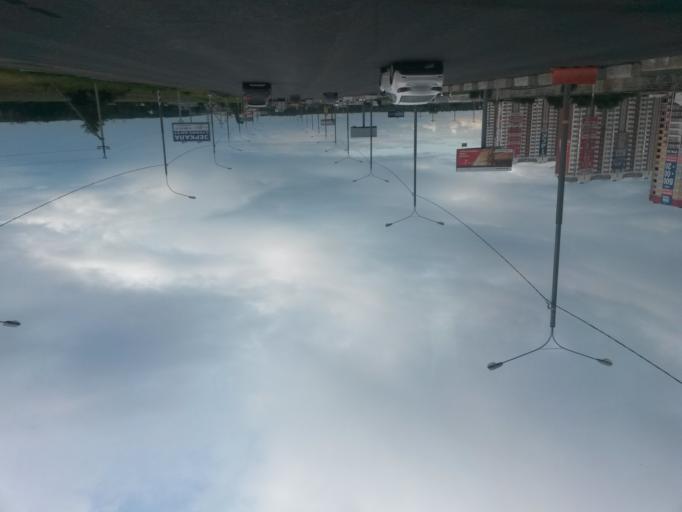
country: RU
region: Moscow
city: Annino
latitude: 55.5354
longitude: 37.6103
